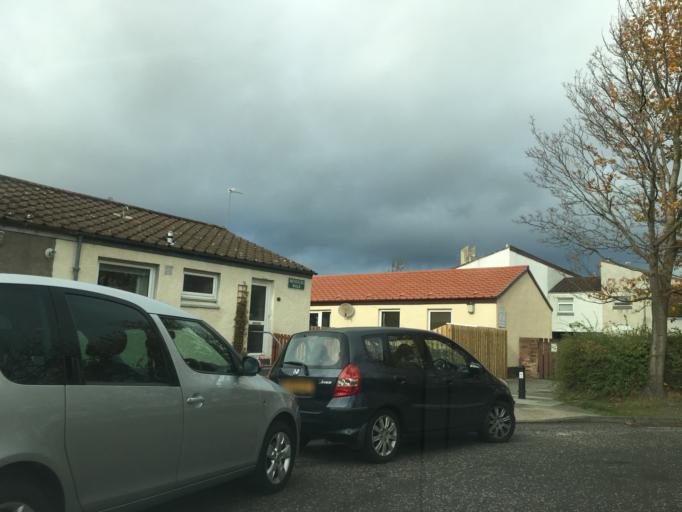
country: GB
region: Scotland
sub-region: Midlothian
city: Loanhead
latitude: 55.9182
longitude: -3.1642
